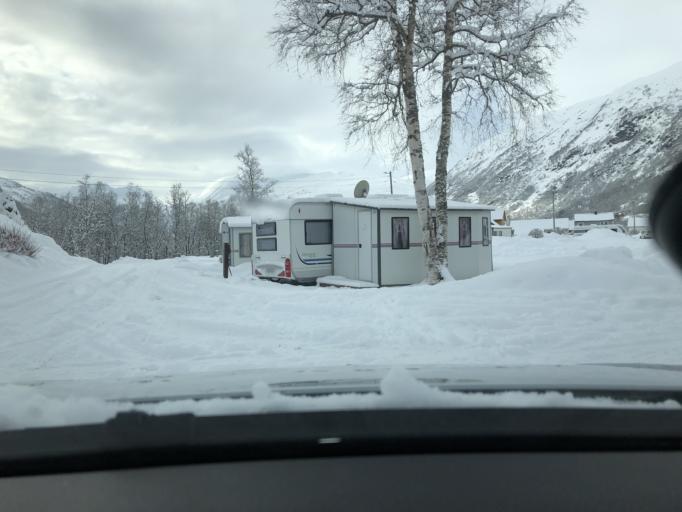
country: NO
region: Hordaland
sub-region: Odda
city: Odda
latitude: 59.8311
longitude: 6.8280
